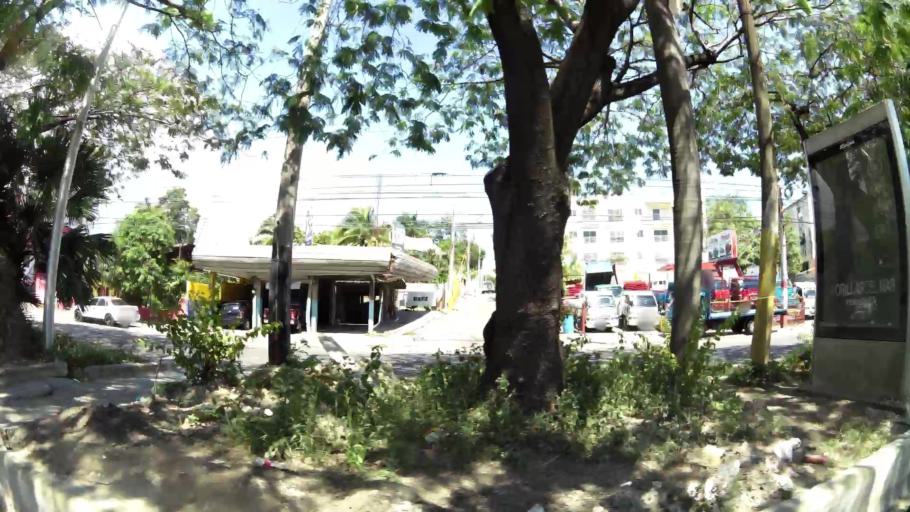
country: DO
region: San Cristobal
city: El Carril
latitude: 18.4628
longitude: -69.9930
